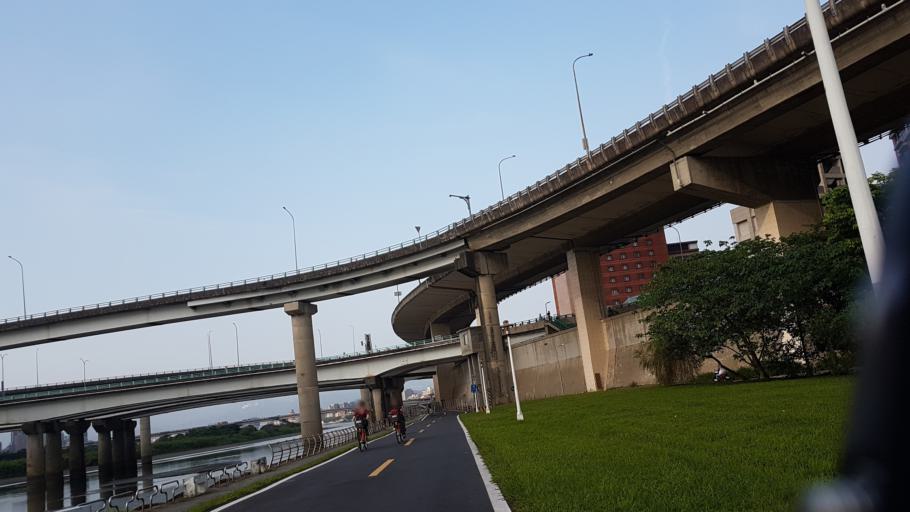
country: TW
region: Taipei
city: Taipei
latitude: 25.0433
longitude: 121.4999
